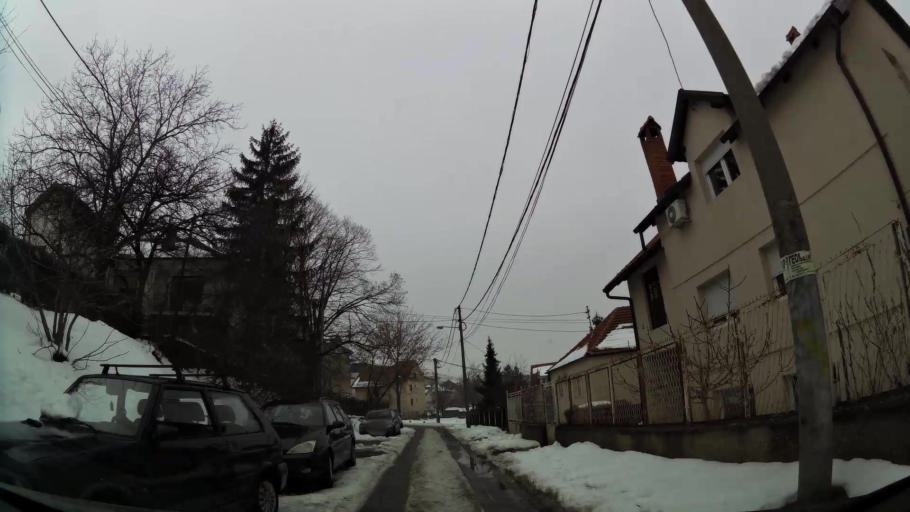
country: RS
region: Central Serbia
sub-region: Belgrade
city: Zvezdara
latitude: 44.7430
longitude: 20.5043
